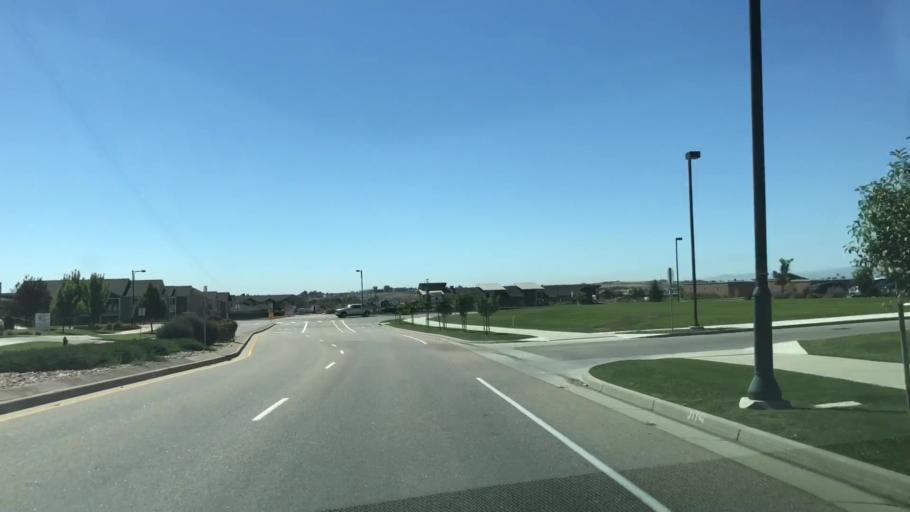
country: US
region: Colorado
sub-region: Weld County
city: Johnstown
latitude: 40.4047
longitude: -104.9740
